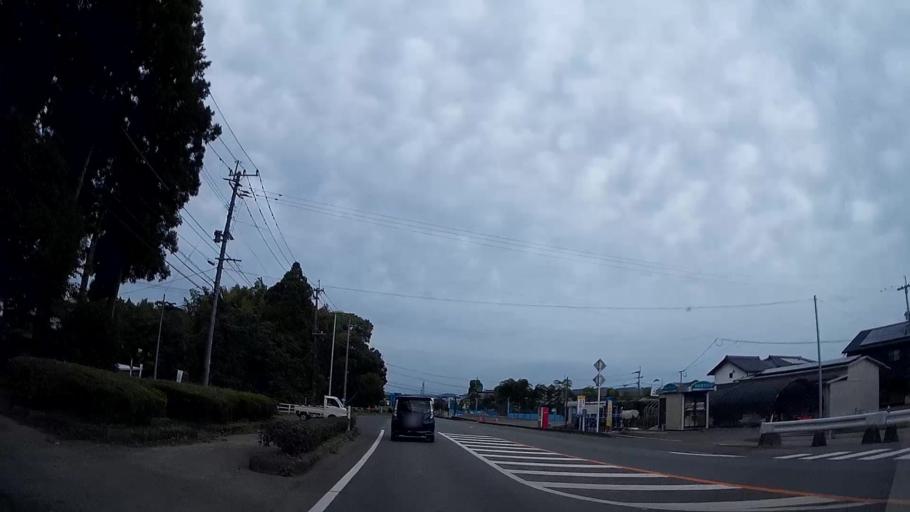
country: JP
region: Kumamoto
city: Kikuchi
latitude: 32.9587
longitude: 130.8202
